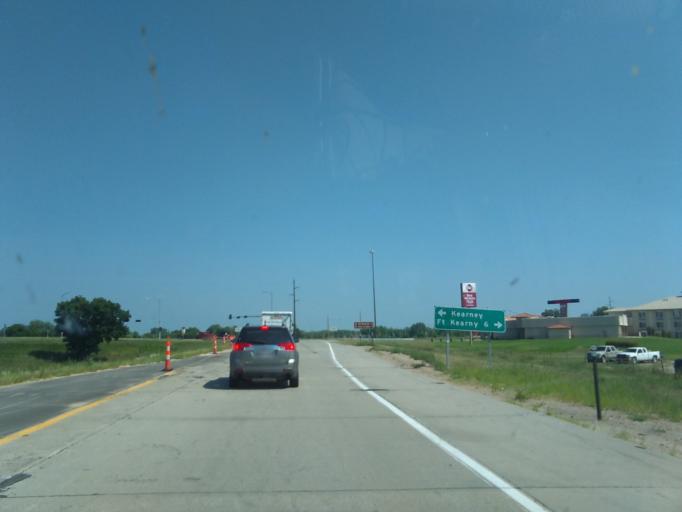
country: US
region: Nebraska
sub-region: Buffalo County
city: Kearney
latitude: 40.6683
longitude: -99.0877
